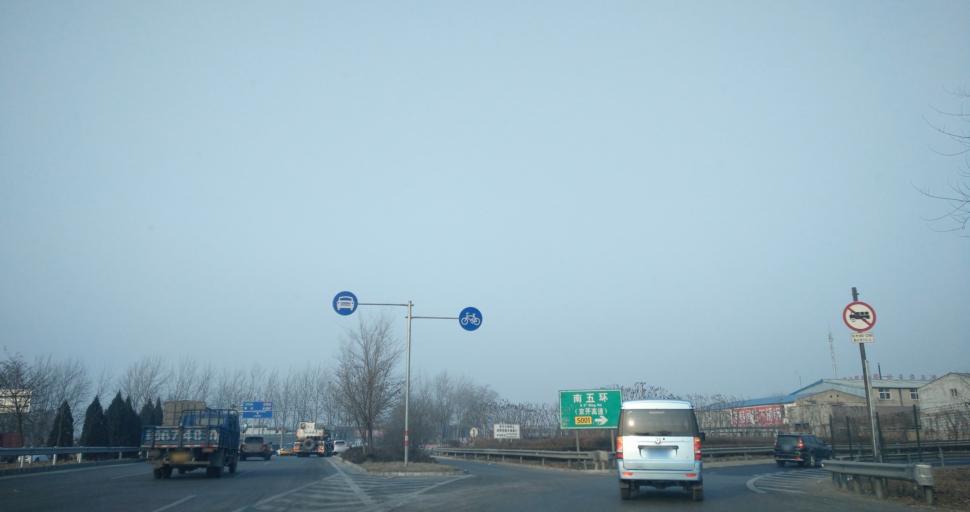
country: CN
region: Beijing
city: Yinghai
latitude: 39.7631
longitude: 116.3957
